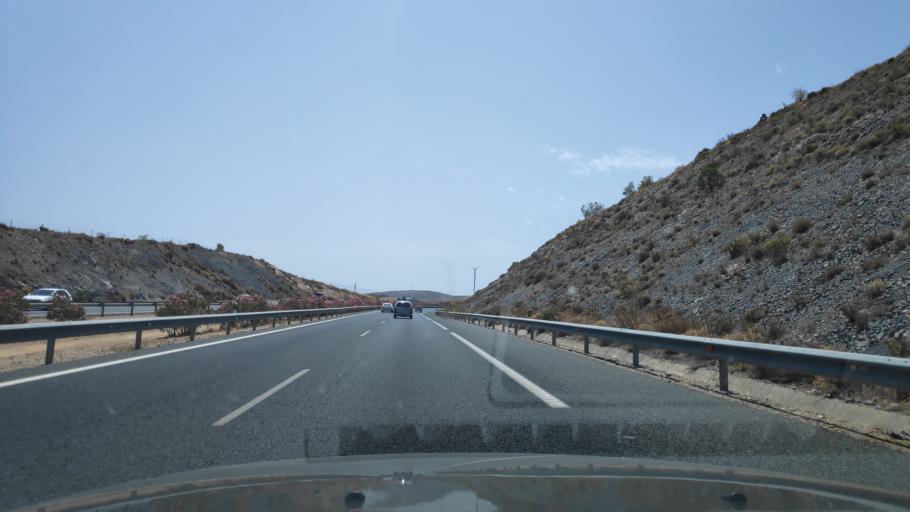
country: ES
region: Andalusia
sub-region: Provincia de Granada
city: Padul
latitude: 37.0209
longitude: -3.6427
